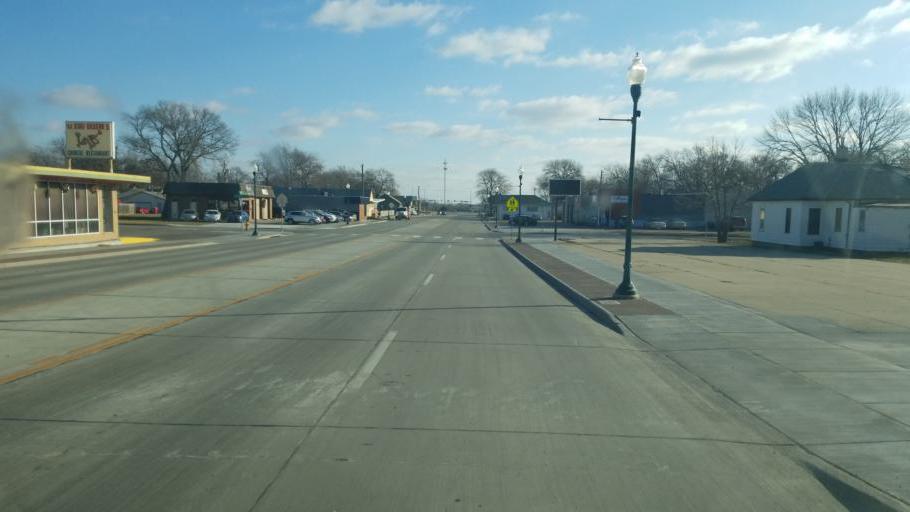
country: US
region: South Dakota
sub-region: Yankton County
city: Yankton
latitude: 42.8710
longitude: -97.3883
